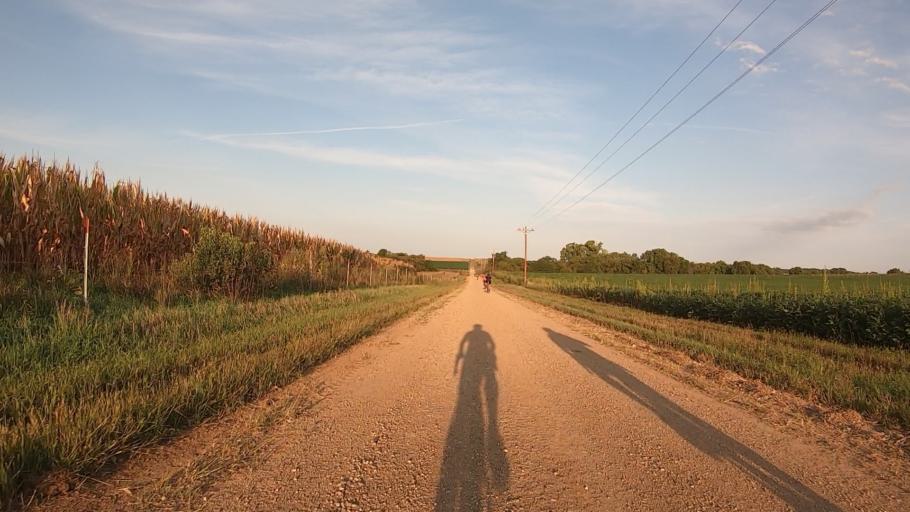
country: US
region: Kansas
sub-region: Marshall County
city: Marysville
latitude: 39.7694
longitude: -96.7155
